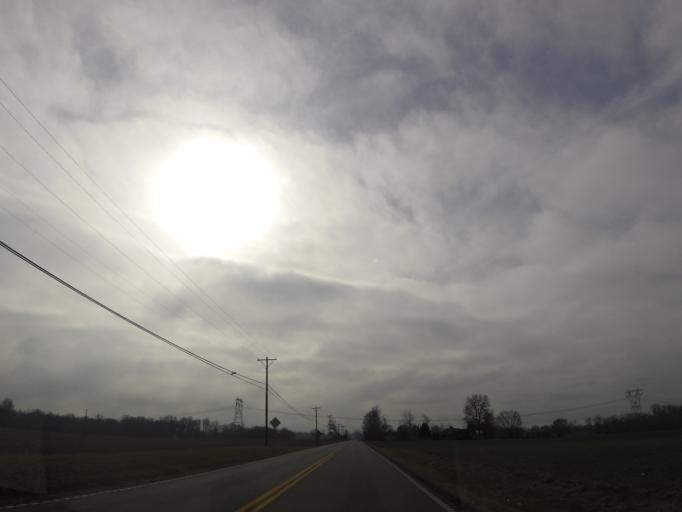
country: US
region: Kentucky
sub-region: Trimble County
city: Bedford
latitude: 38.6560
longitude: -85.3192
